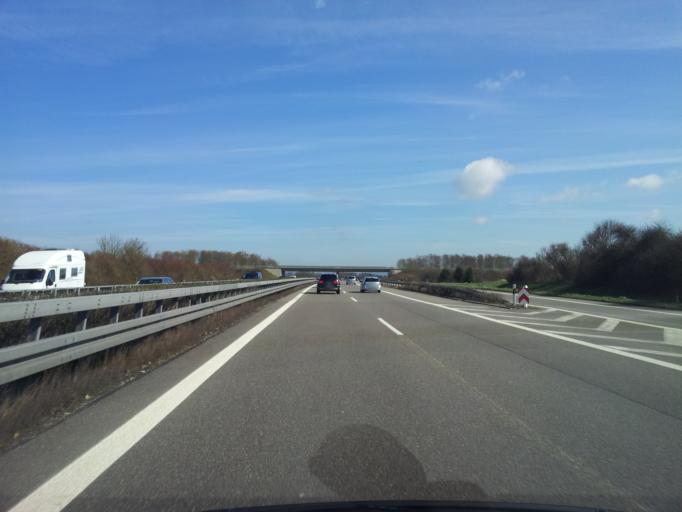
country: DE
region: Baden-Wuerttemberg
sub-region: Regierungsbezirk Stuttgart
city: Bondorf
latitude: 48.5002
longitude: 8.8393
